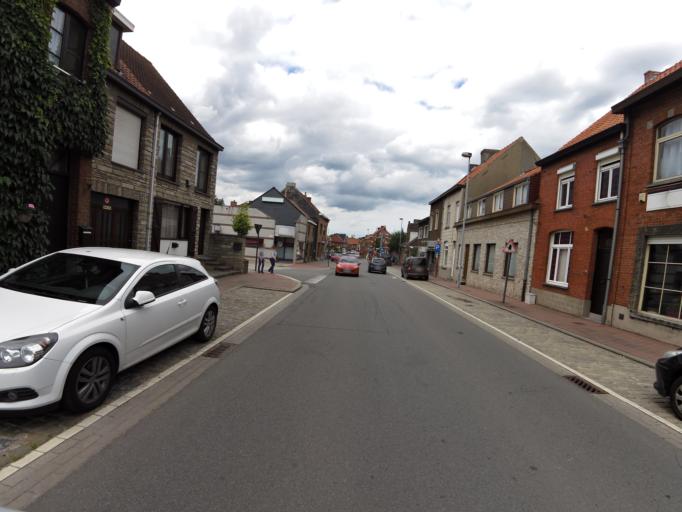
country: BE
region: Flanders
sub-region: Provincie West-Vlaanderen
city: Kortemark
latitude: 51.0244
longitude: 3.0432
